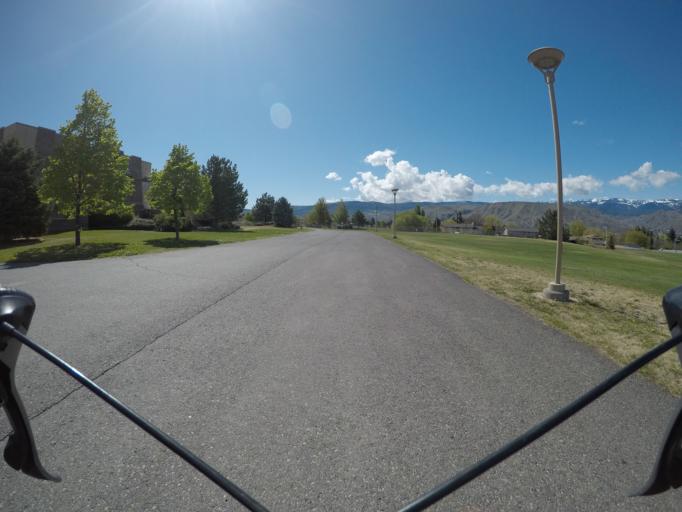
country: US
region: Washington
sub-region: Douglas County
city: East Wenatchee Bench
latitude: 47.4179
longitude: -120.2741
